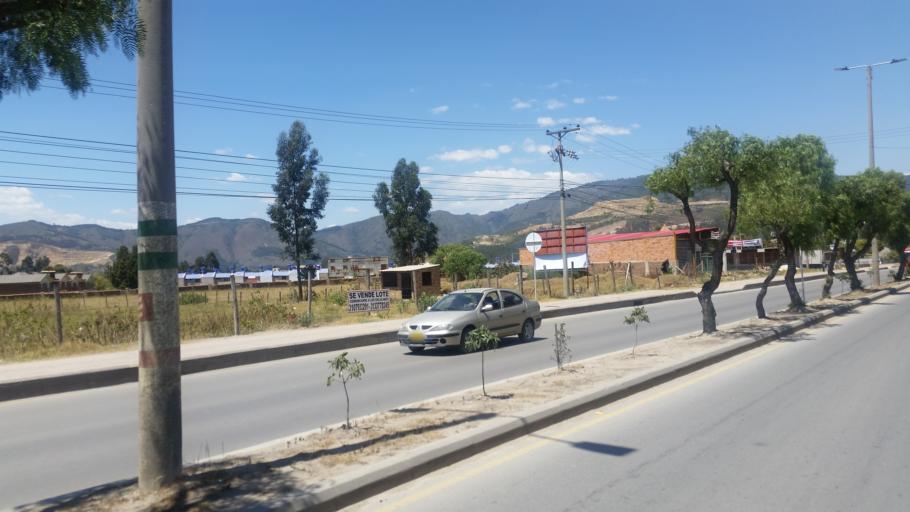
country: CO
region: Boyaca
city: Sogamoso
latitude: 5.7435
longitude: -72.9149
